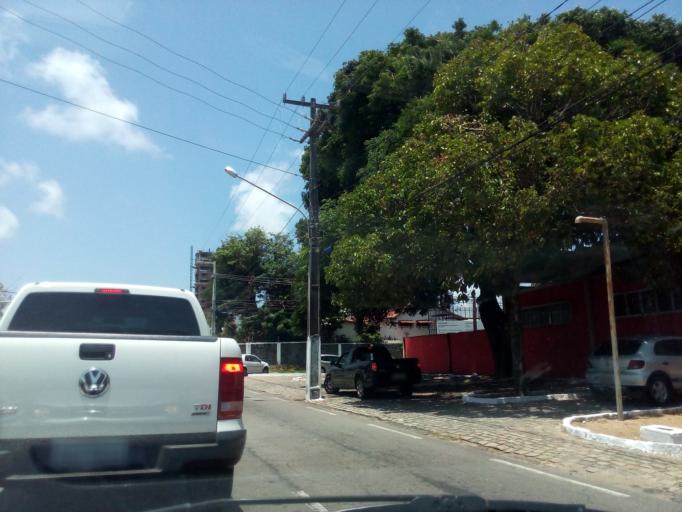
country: BR
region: Rio Grande do Norte
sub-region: Natal
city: Natal
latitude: -5.8269
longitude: -35.2071
